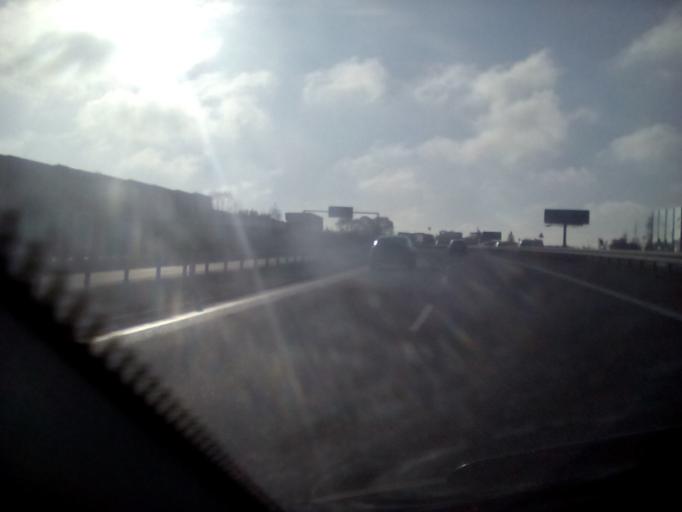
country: PL
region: Masovian Voivodeship
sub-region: Powiat grojecki
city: Grojec
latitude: 51.8639
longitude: 20.8512
